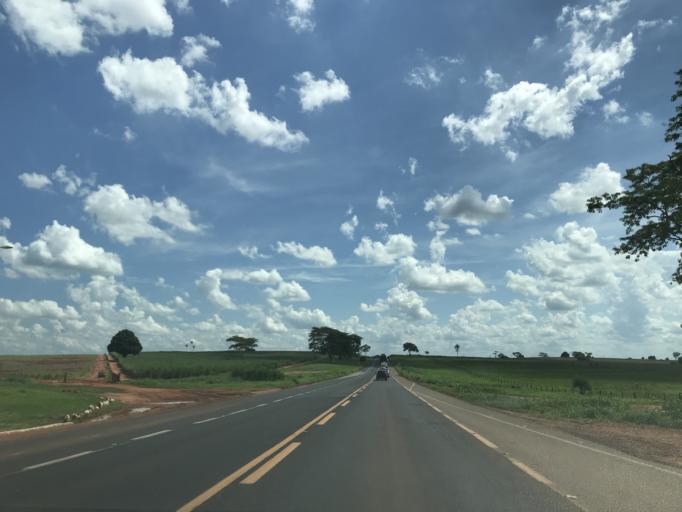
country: BR
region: Sao Paulo
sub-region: Nova Granada
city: Nova Granada
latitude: -20.4492
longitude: -49.2834
